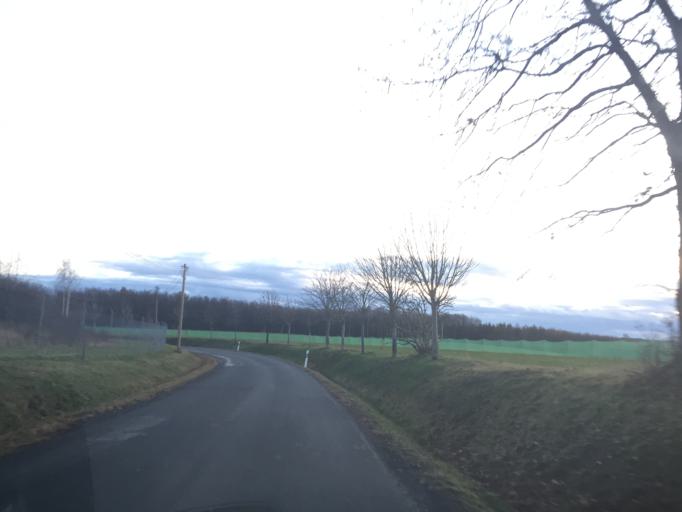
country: DE
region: Thuringia
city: Schmolln
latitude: 50.9010
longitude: 12.3320
